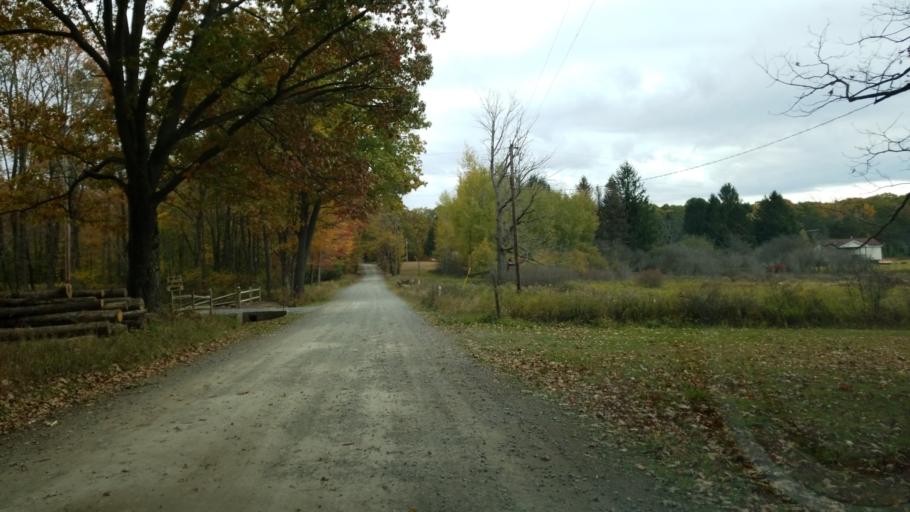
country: US
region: Pennsylvania
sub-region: Clearfield County
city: Shiloh
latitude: 41.1873
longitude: -78.3627
